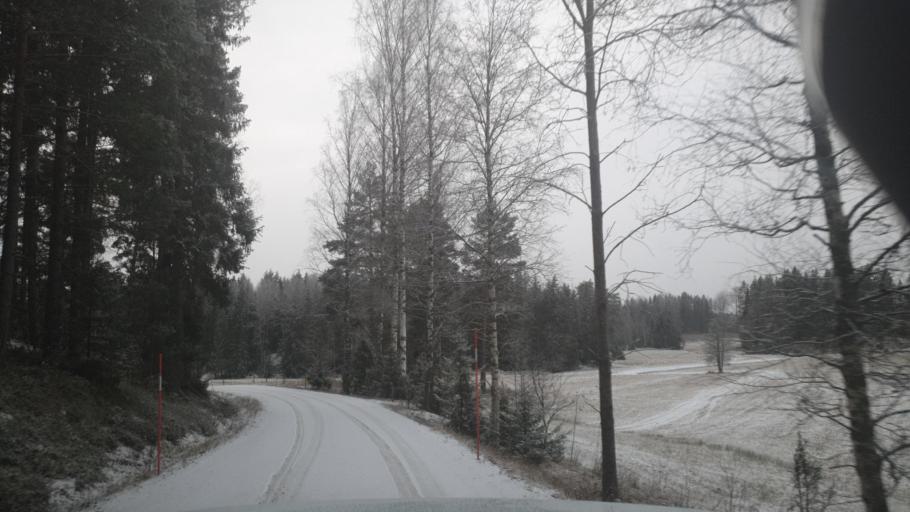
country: SE
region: Vaermland
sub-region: Grums Kommun
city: Grums
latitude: 59.5117
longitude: 12.9271
